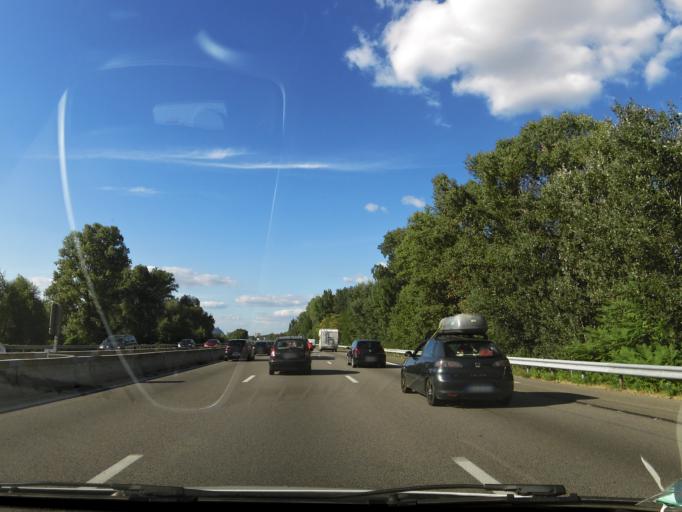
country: FR
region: Rhone-Alpes
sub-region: Departement de la Drome
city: Portes-les-Valence
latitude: 44.8565
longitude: 4.8669
